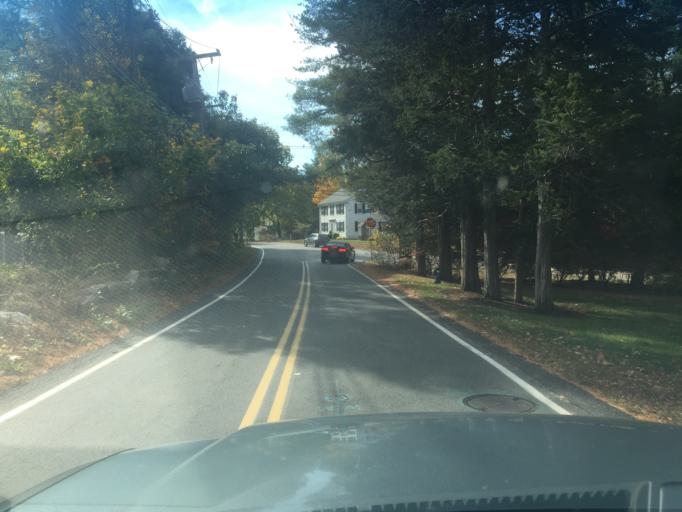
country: US
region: Massachusetts
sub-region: Norfolk County
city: Medway
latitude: 42.1522
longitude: -71.4254
